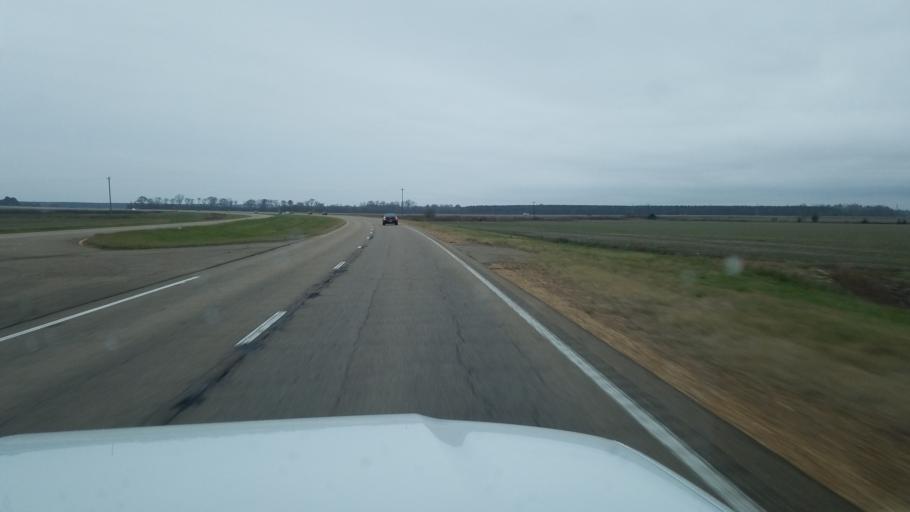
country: US
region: Mississippi
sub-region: Chickasaw County
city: Okolona
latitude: 33.9372
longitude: -88.7337
